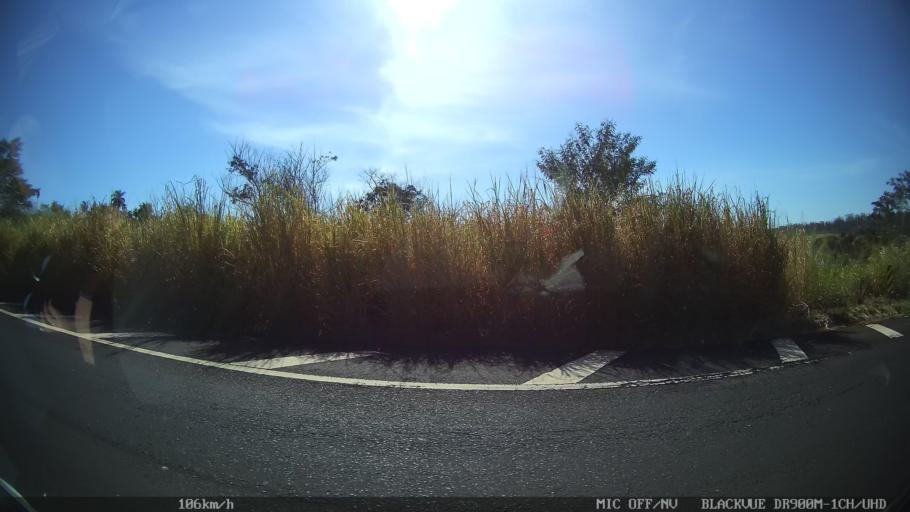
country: BR
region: Sao Paulo
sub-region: Barretos
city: Barretos
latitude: -20.6031
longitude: -48.7330
